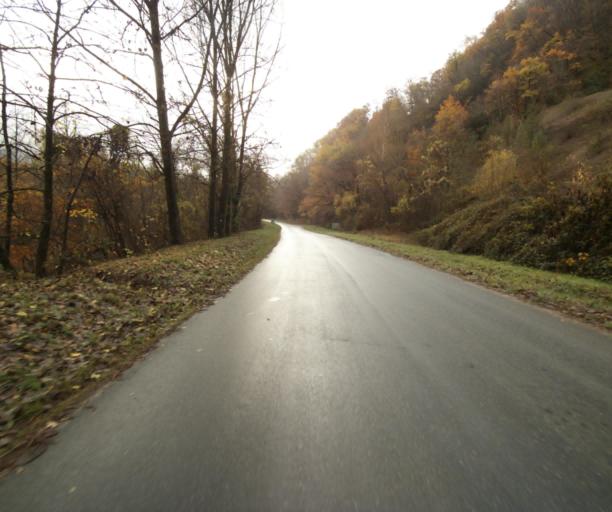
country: FR
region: Limousin
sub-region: Departement de la Correze
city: Cornil
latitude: 45.1895
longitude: 1.6515
